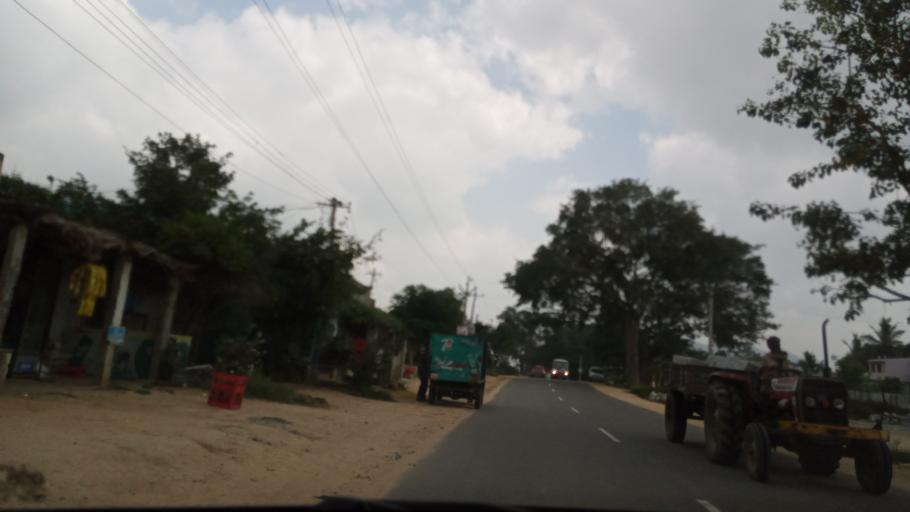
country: IN
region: Andhra Pradesh
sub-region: Chittoor
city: Madanapalle
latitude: 13.6430
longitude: 78.5689
